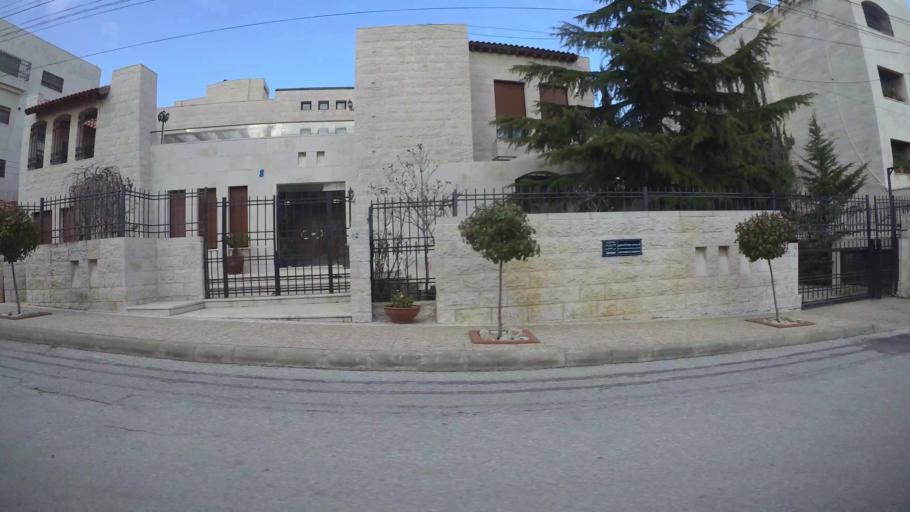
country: JO
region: Amman
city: Al Jubayhah
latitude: 31.9800
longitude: 35.8600
